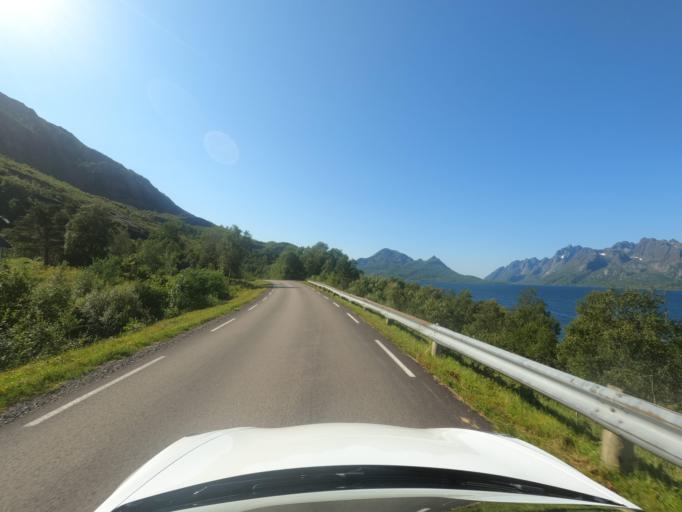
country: NO
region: Nordland
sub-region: Hadsel
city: Stokmarknes
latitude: 68.3304
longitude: 15.0164
